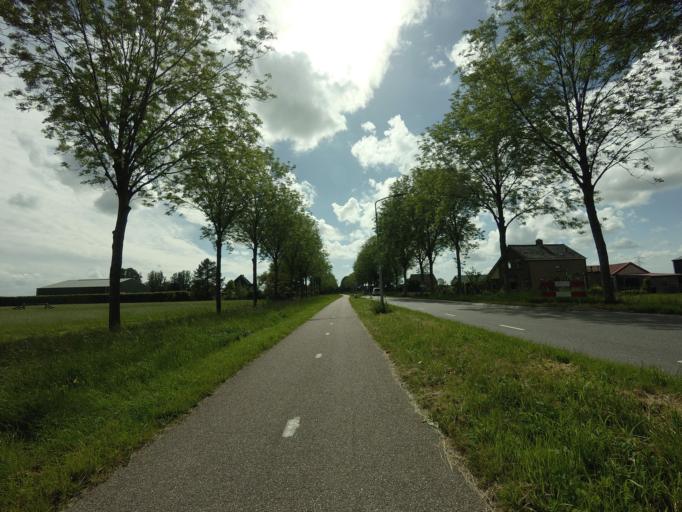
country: NL
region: North Holland
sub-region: Gemeente Hoorn
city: Hoorn
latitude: 52.6789
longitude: 5.0649
